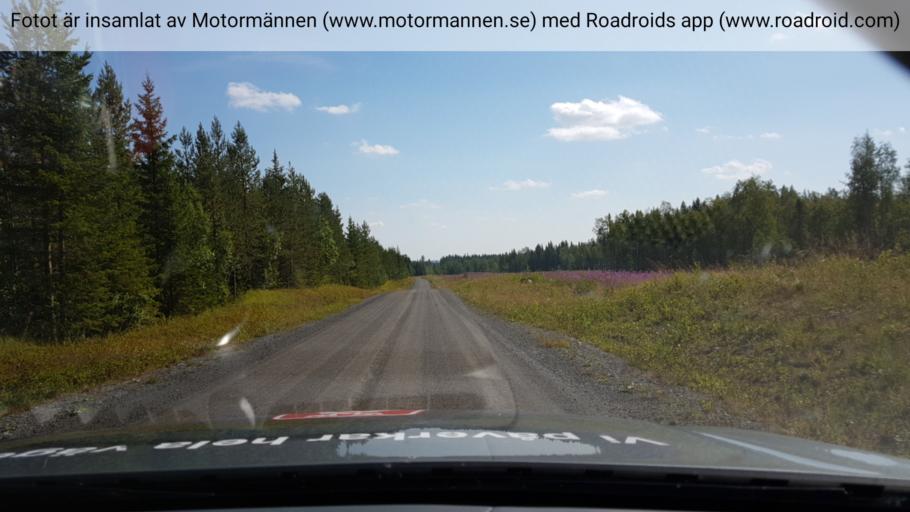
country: SE
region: Jaemtland
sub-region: OEstersunds Kommun
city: Lit
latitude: 63.3523
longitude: 15.2275
